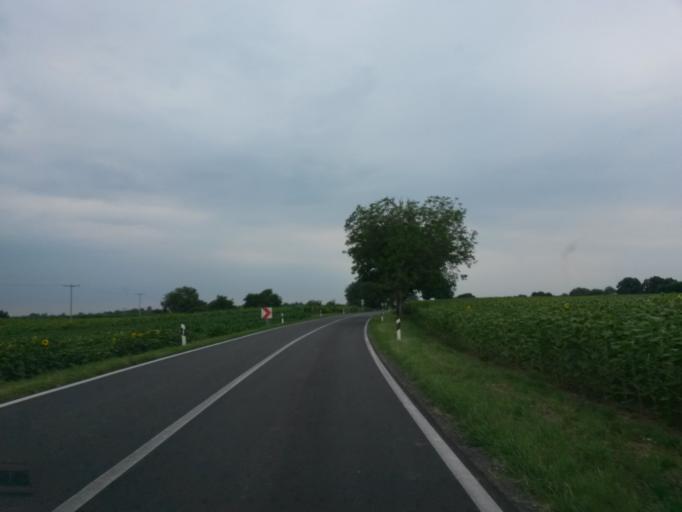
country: HR
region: Vukovarsko-Srijemska
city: Lovas
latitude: 45.2465
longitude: 19.2250
